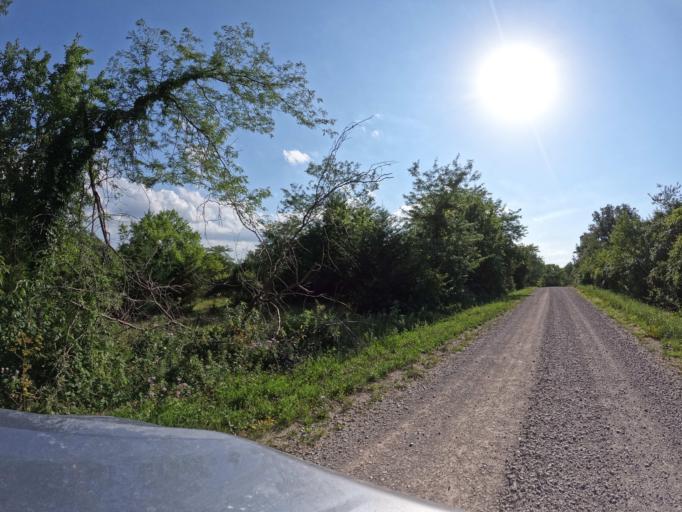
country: US
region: Iowa
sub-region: Appanoose County
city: Centerville
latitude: 40.7321
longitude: -93.0192
